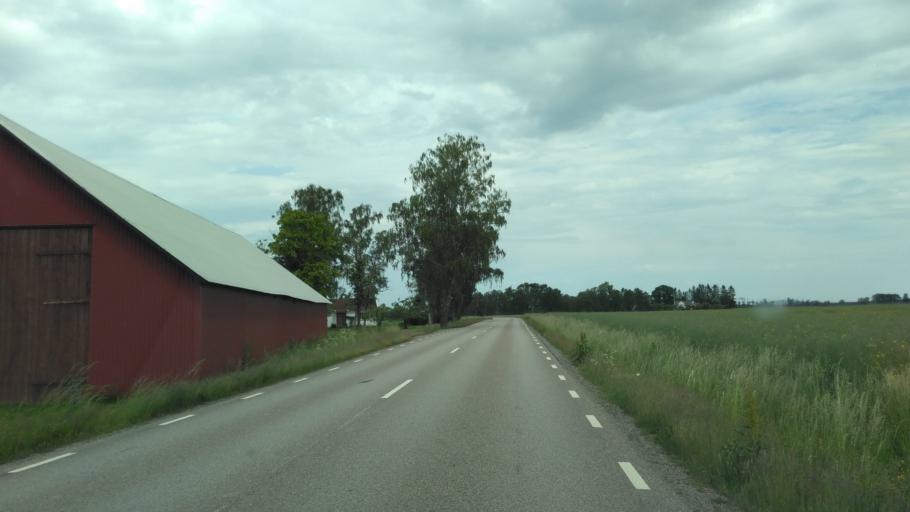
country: SE
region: Vaestra Goetaland
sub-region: Lidkopings Kommun
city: Lidkoping
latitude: 58.4134
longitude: 13.1635
